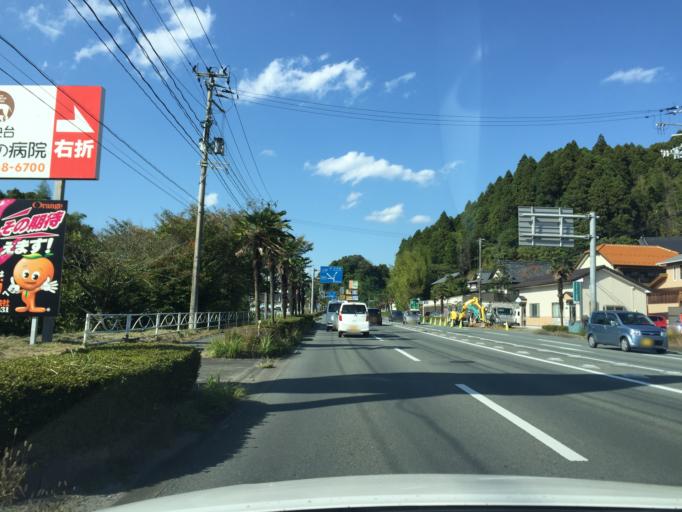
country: JP
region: Fukushima
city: Iwaki
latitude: 37.0170
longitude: 140.9029
